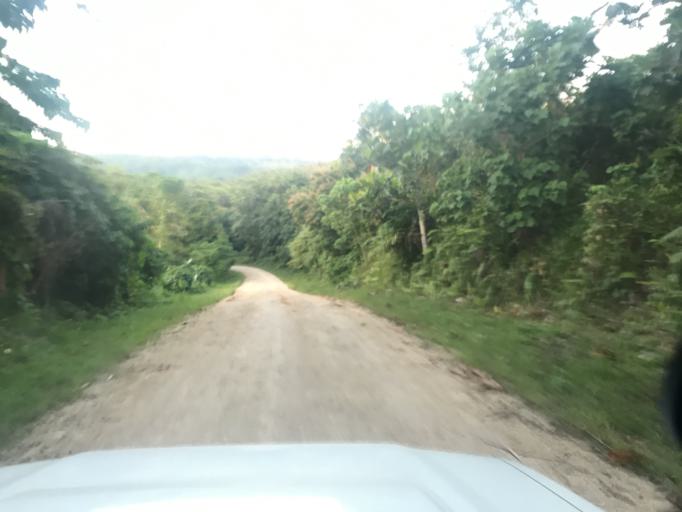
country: VU
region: Sanma
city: Luganville
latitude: -15.5586
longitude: 166.9669
